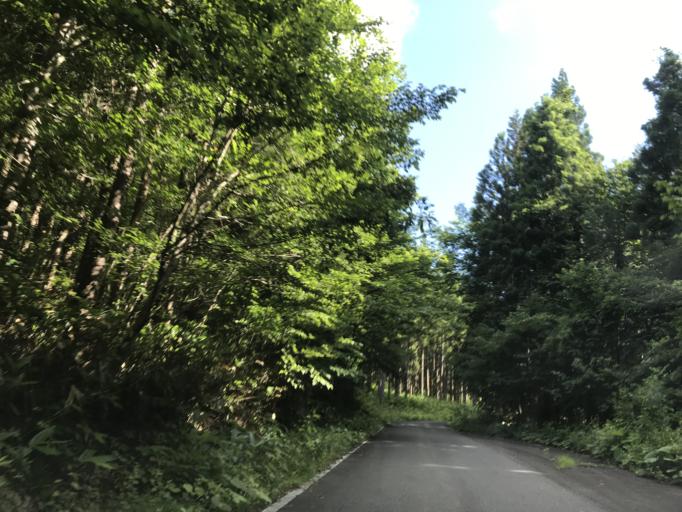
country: JP
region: Iwate
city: Ichinoseki
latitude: 38.8957
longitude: 140.9080
